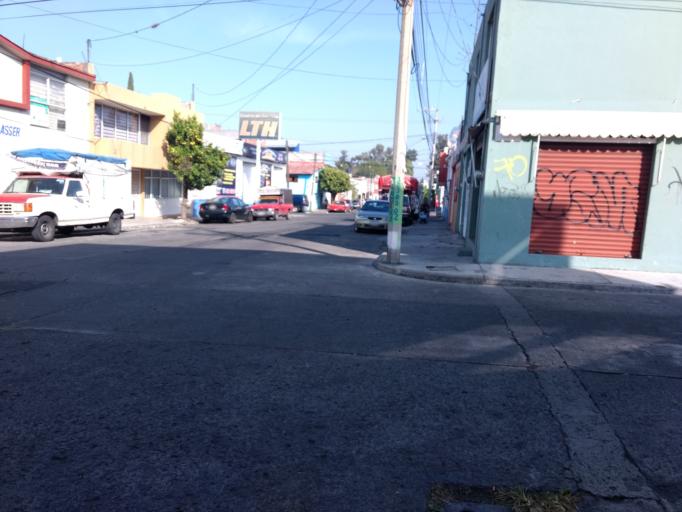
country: MX
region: Michoacan
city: Morelia
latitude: 19.7036
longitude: -101.2107
